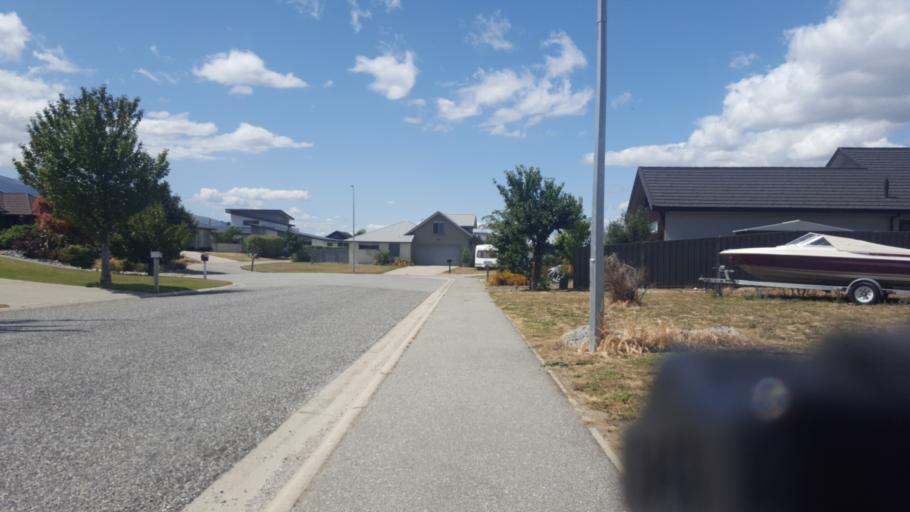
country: NZ
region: Otago
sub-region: Queenstown-Lakes District
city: Wanaka
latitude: -44.9717
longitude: 169.2488
